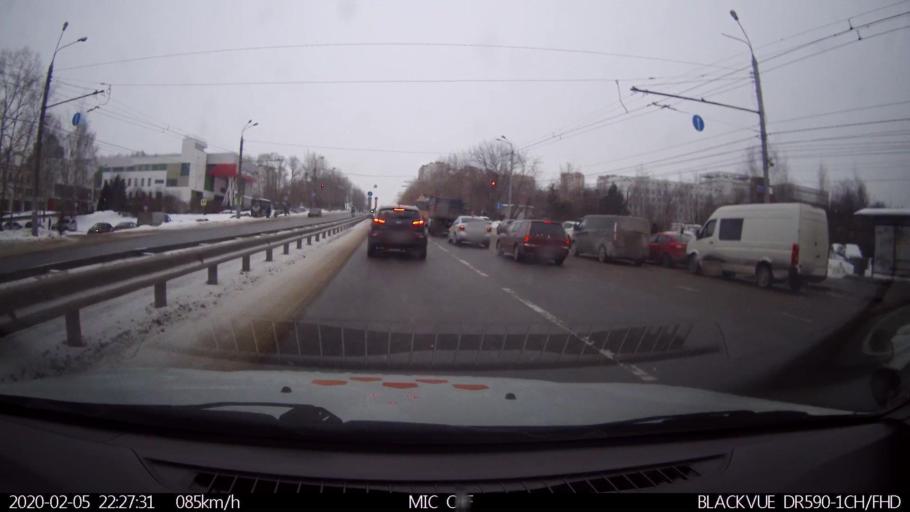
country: RU
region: Nizjnij Novgorod
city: Imeni Stepana Razina
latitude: 54.7609
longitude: 44.1155
